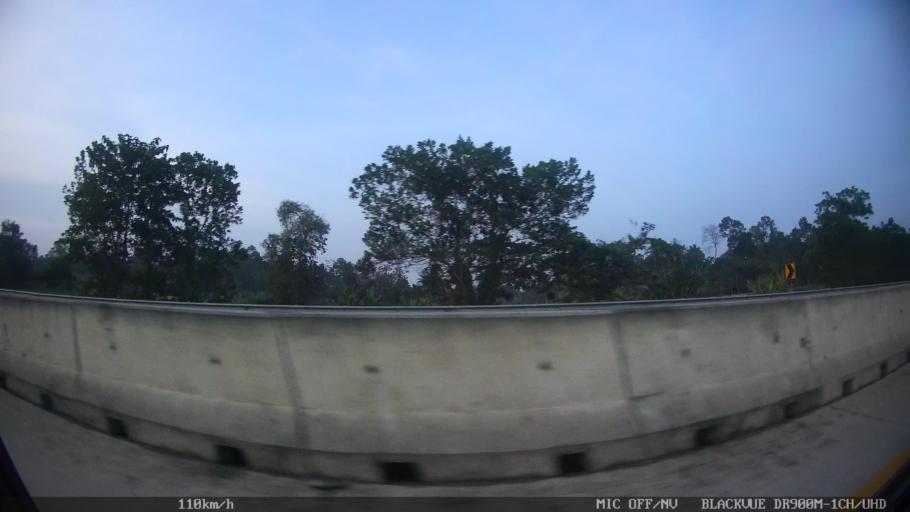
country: ID
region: Lampung
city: Pasuruan
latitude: -5.7331
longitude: 105.6845
